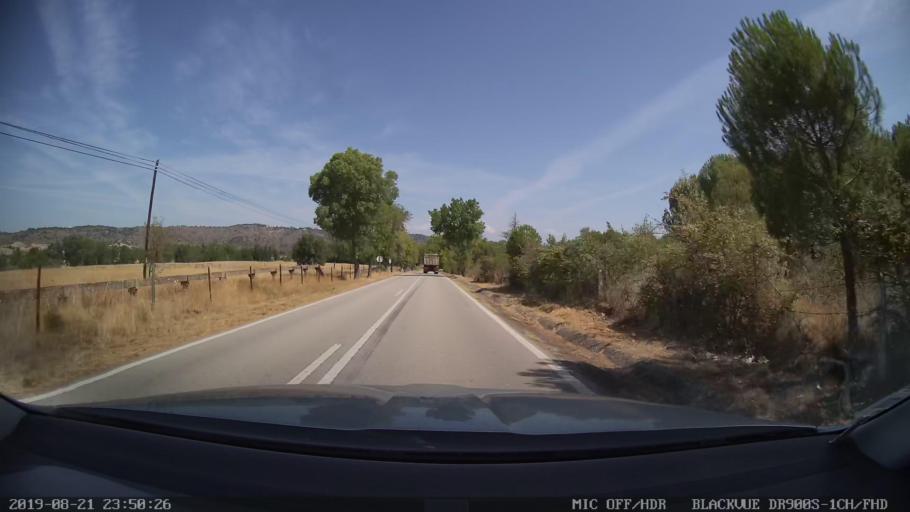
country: PT
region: Castelo Branco
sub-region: Idanha-A-Nova
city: Idanha-a-Nova
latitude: 39.8899
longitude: -7.2425
